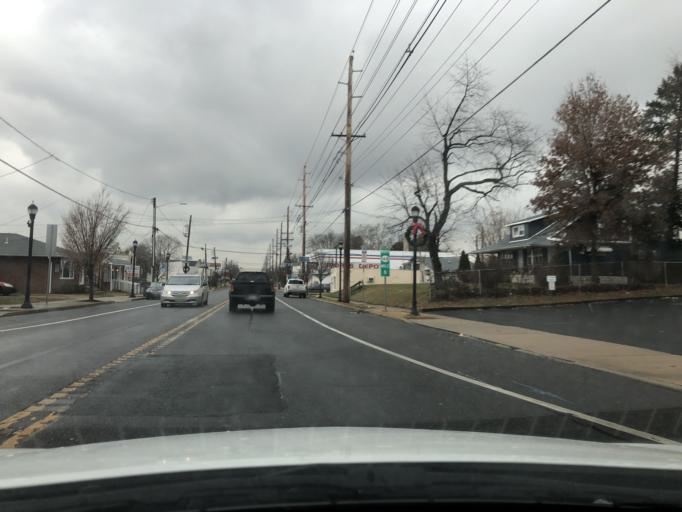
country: US
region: New Jersey
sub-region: Camden County
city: Runnemede
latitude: 39.8531
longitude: -75.0743
